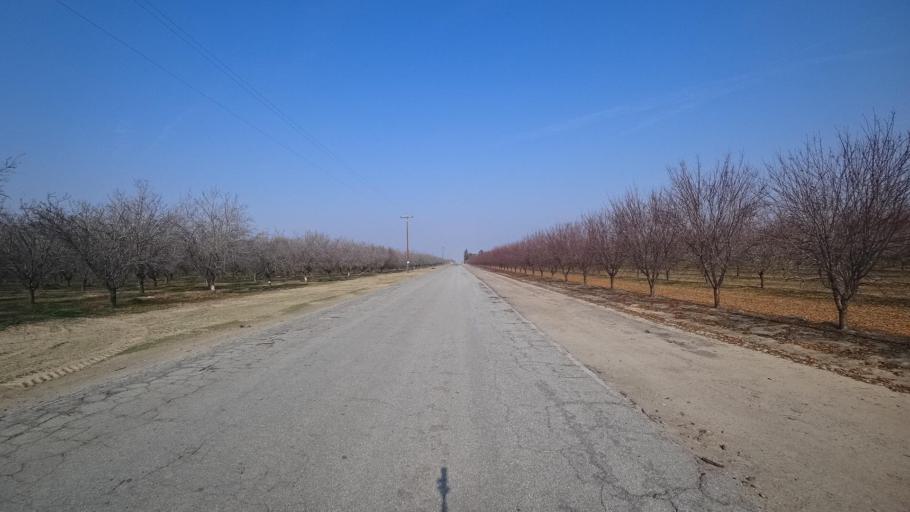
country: US
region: California
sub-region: Kern County
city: Shafter
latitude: 35.3589
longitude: -119.3056
